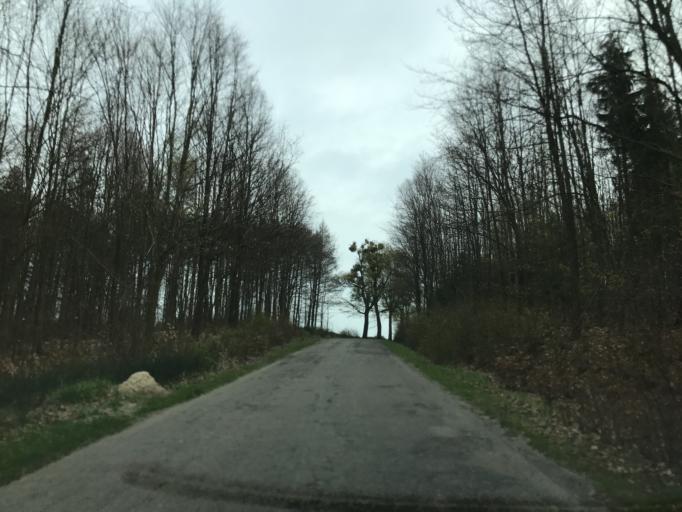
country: PL
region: Warmian-Masurian Voivodeship
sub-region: Powiat ostrodzki
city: Gierzwald
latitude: 53.6417
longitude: 20.0933
